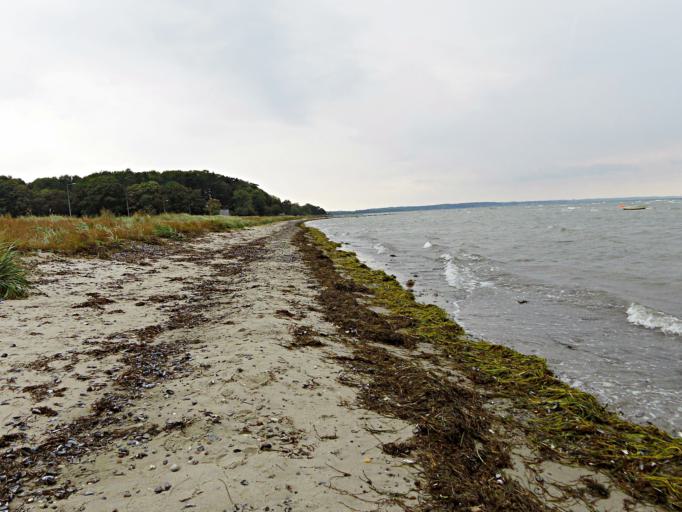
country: DK
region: Capital Region
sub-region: Fredensborg Kommune
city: Kokkedal
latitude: 55.9031
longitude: 12.5305
